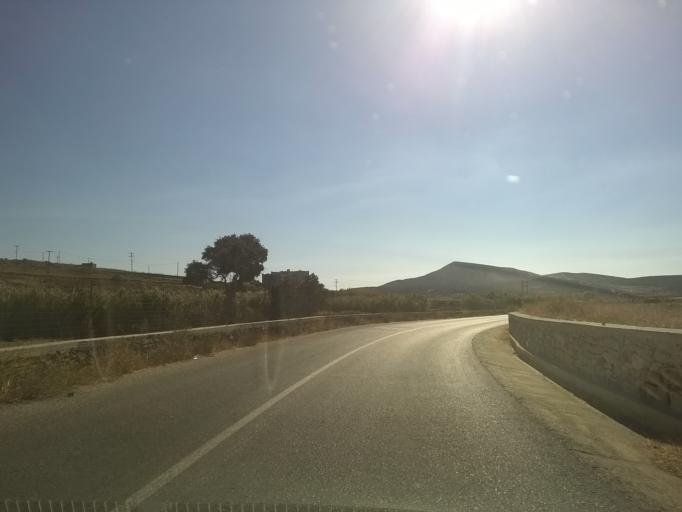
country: GR
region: South Aegean
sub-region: Nomos Kykladon
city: Filotion
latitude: 37.0457
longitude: 25.4308
